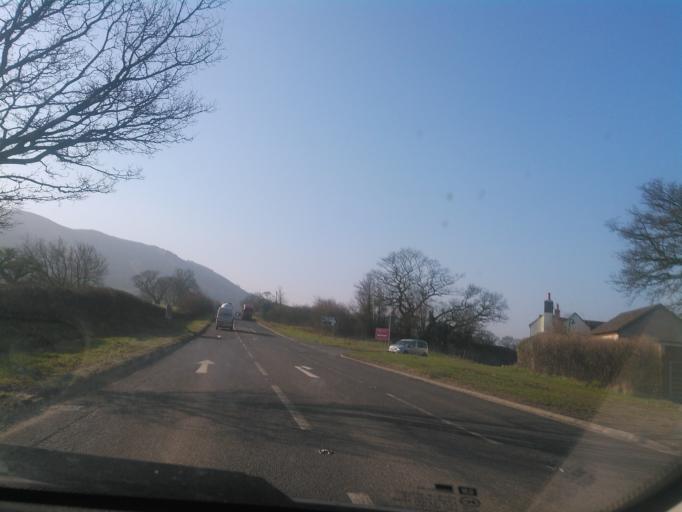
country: GB
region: England
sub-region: Shropshire
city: Church Stretton
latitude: 52.5665
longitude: -2.7819
